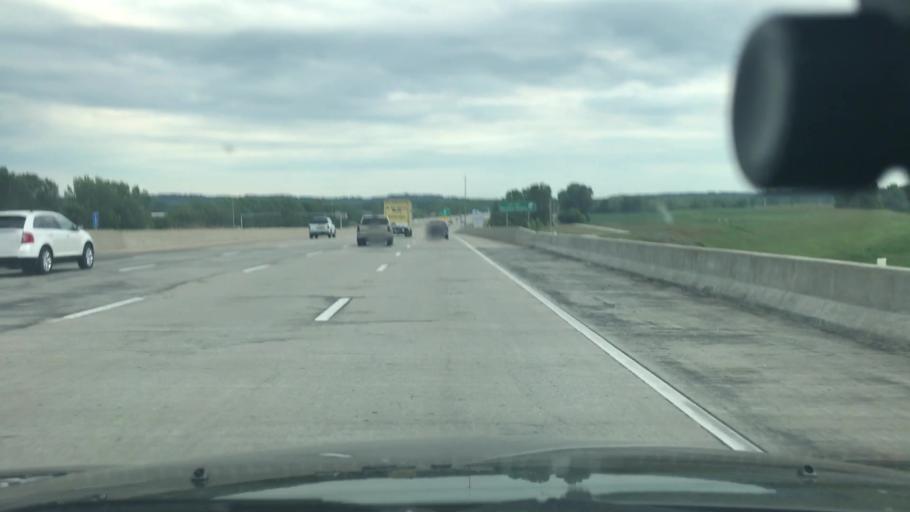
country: US
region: Missouri
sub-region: Saint Charles County
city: Saint Charles
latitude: 38.7312
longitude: -90.5183
